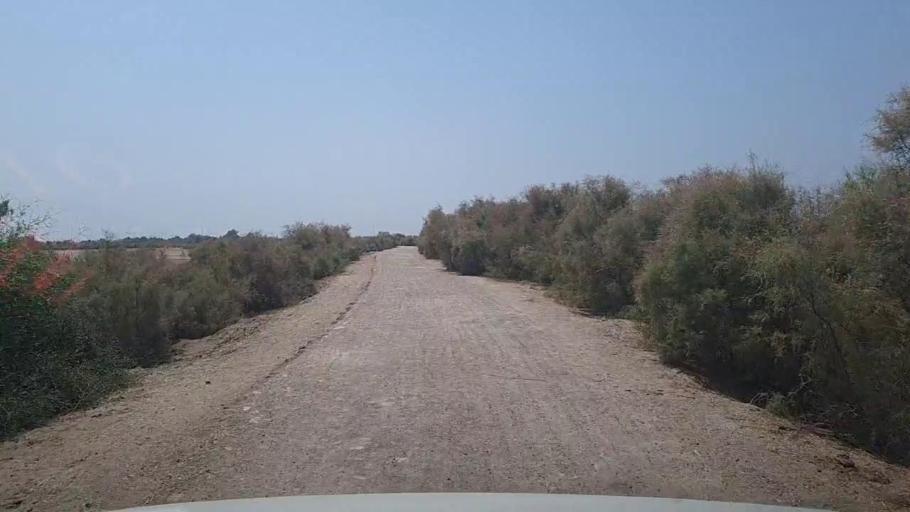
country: PK
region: Sindh
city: Kandhkot
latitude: 28.3110
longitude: 69.3583
